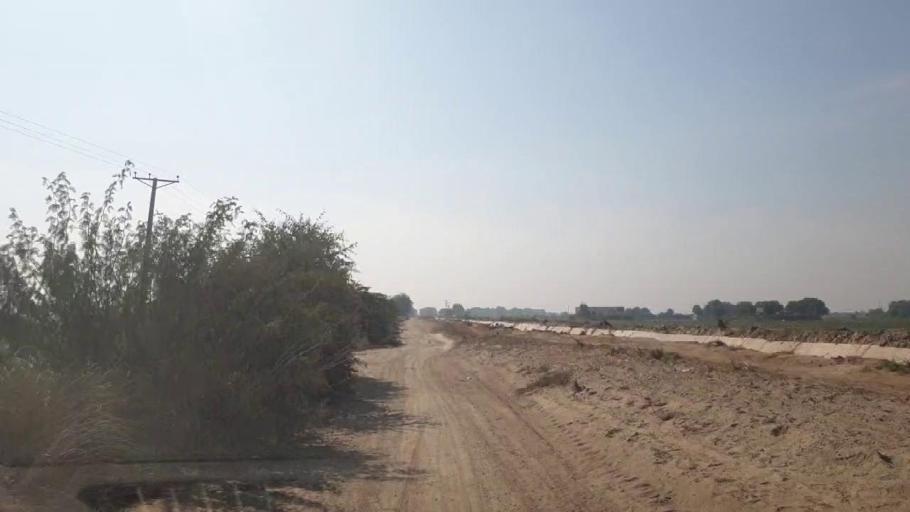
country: PK
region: Sindh
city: Matiari
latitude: 25.6668
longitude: 68.3463
